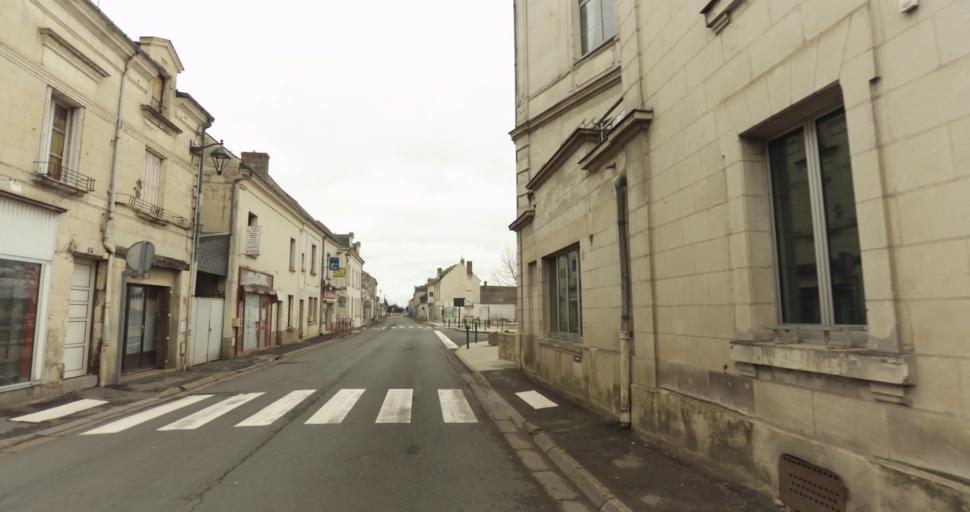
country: FR
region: Pays de la Loire
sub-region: Departement de Maine-et-Loire
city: Allonnes
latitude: 47.2932
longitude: 0.0236
